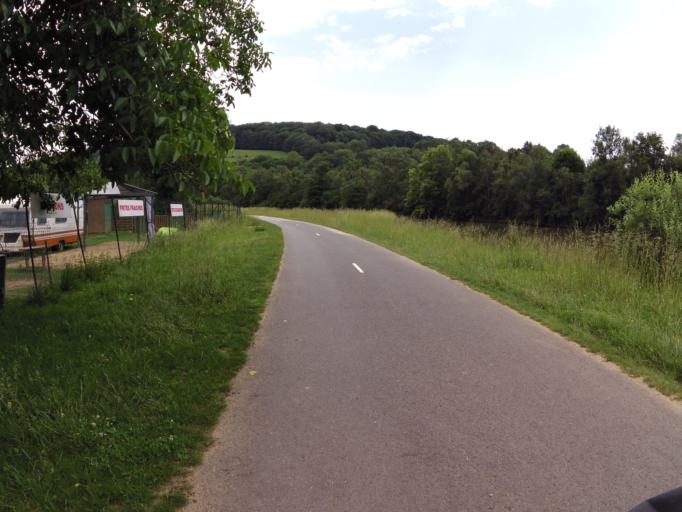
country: FR
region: Champagne-Ardenne
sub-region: Departement des Ardennes
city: Montcy-Notre-Dame
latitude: 49.7709
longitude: 4.7432
